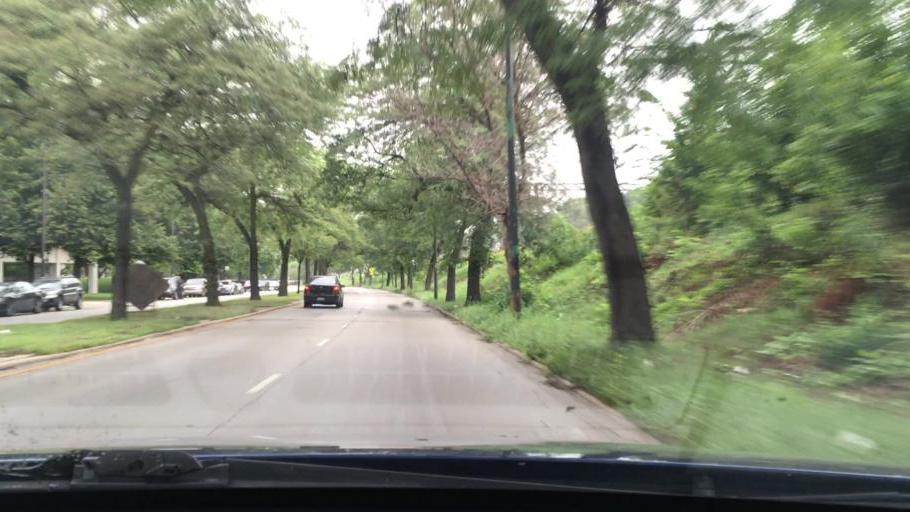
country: US
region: Illinois
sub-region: Cook County
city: Chicago
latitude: 41.8063
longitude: -87.5894
